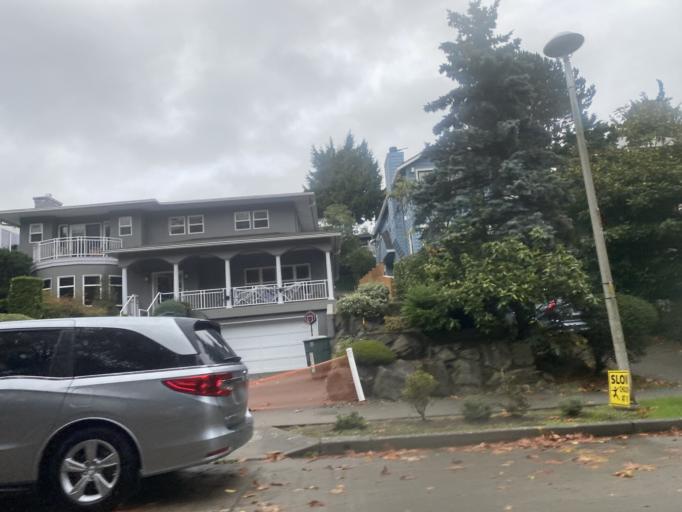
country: US
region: Washington
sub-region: King County
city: Seattle
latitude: 47.6480
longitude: -122.4142
